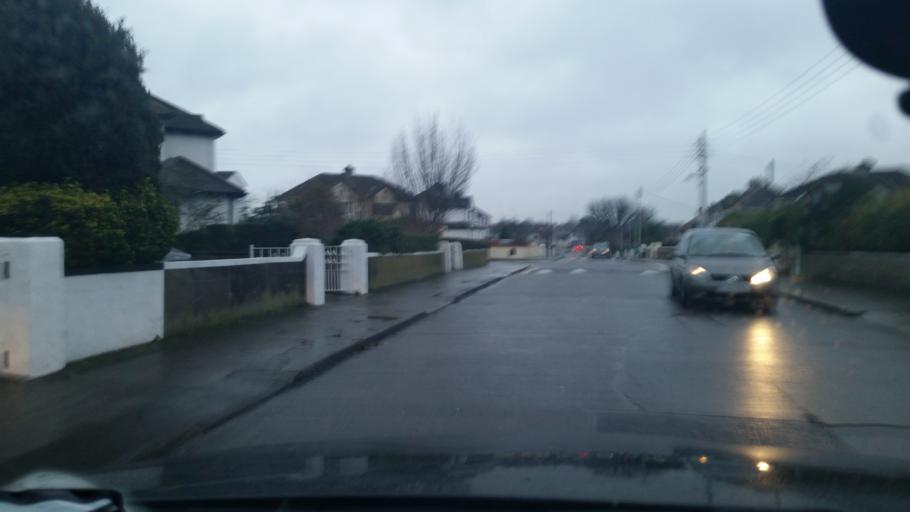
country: IE
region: Leinster
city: Marino
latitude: 53.3792
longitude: -6.2298
